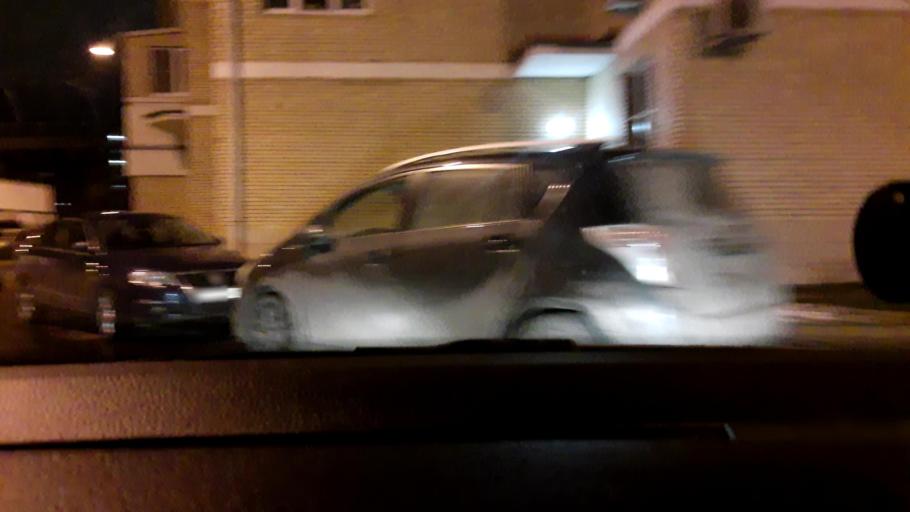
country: RU
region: Moscow
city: Yaroslavskiy
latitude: 55.8837
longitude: 37.7059
